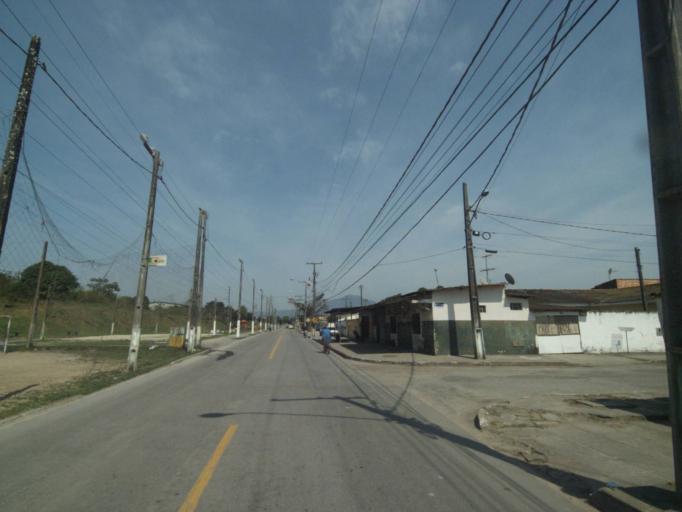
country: BR
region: Parana
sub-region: Paranagua
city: Paranagua
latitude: -25.5420
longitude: -48.5462
